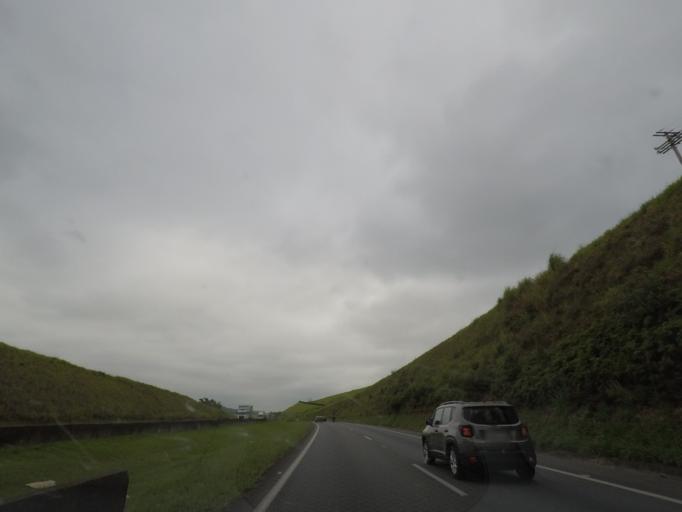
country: BR
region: Sao Paulo
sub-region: Itatiba
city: Itatiba
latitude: -23.0124
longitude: -46.7640
